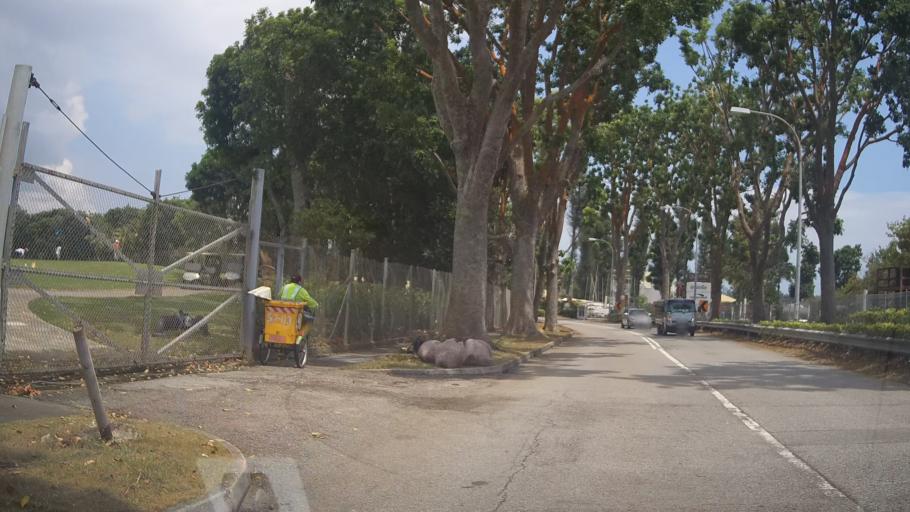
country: SG
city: Singapore
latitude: 1.3170
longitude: 103.9766
